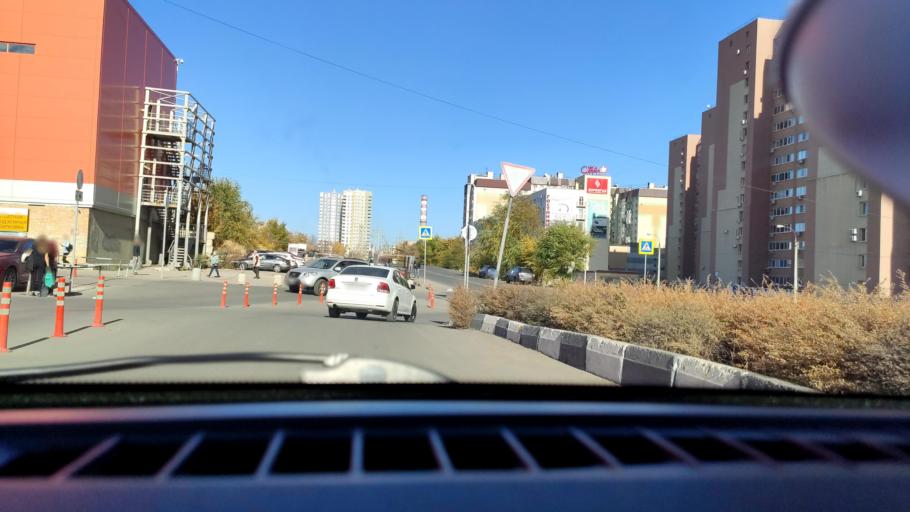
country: RU
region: Samara
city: Samara
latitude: 53.2071
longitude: 50.2026
